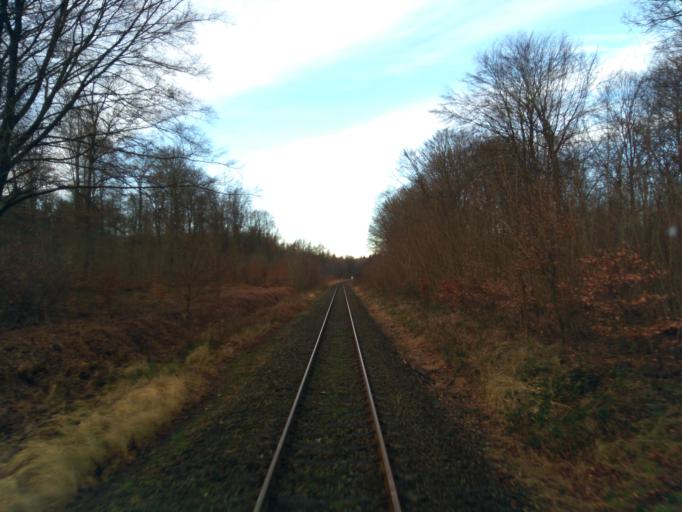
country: DE
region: Lower Saxony
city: Schwienau
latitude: 53.0116
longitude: 10.4644
